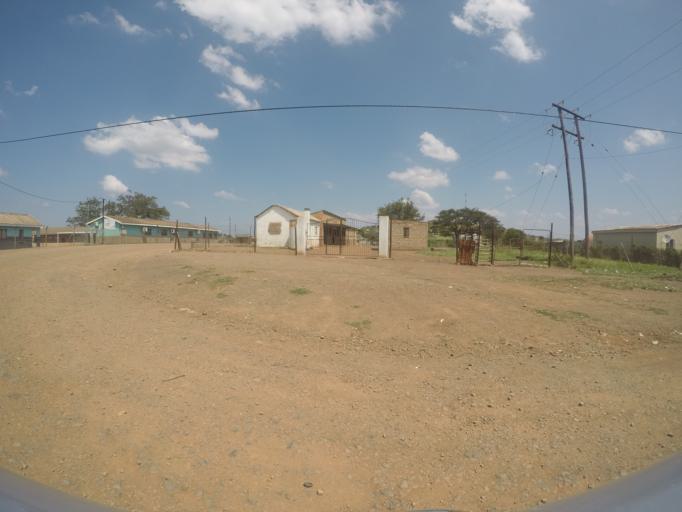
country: ZA
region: KwaZulu-Natal
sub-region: uThungulu District Municipality
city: Empangeni
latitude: -28.5952
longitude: 31.7418
